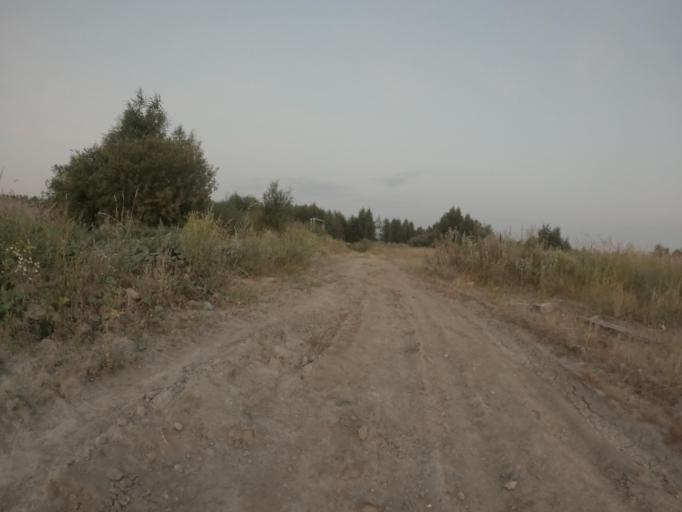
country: RU
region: Leningrad
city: Yanino Vtoroye
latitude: 59.9342
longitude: 30.5959
